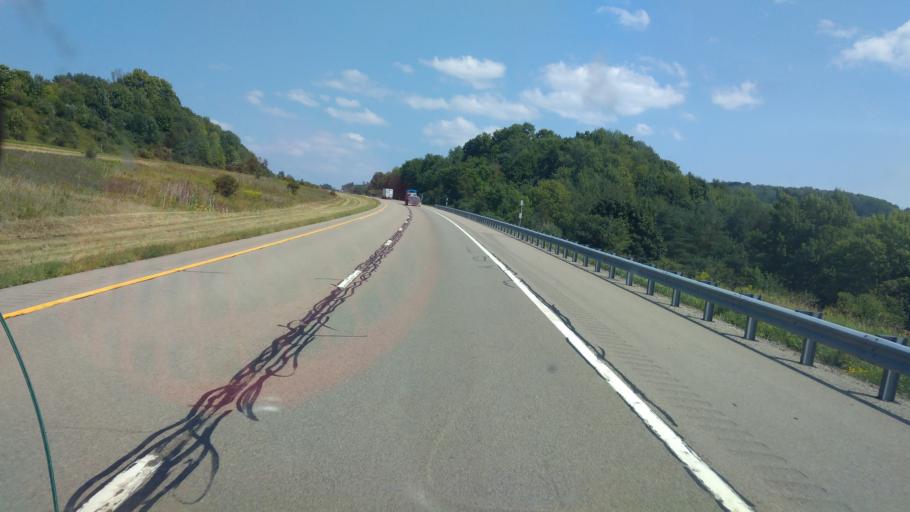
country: US
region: New York
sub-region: Steuben County
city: Hornell
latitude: 42.3743
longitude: -77.5594
